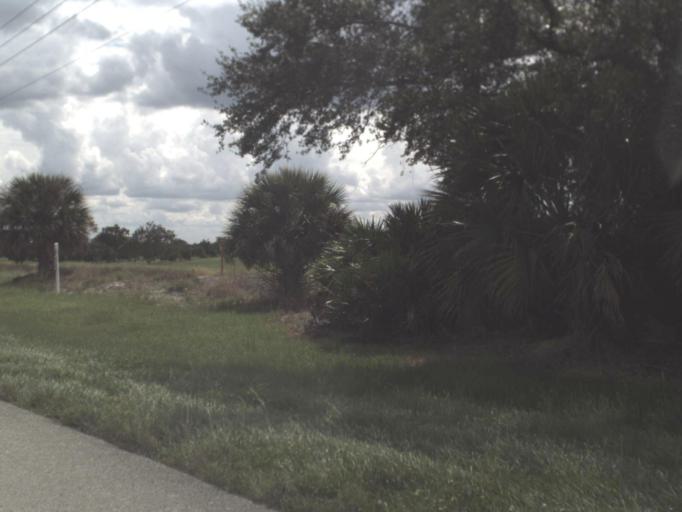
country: US
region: Florida
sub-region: DeSoto County
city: Nocatee
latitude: 27.0342
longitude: -81.7719
